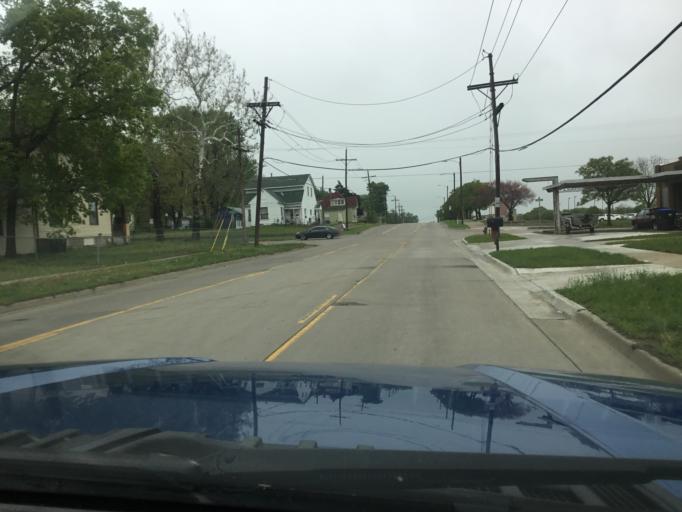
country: US
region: Kansas
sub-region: Shawnee County
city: Topeka
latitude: 39.0369
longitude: -95.6883
